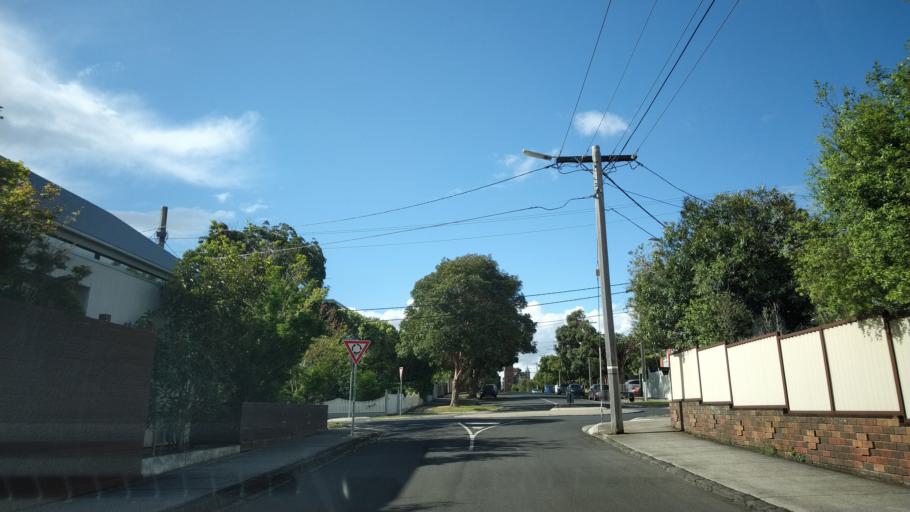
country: AU
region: Victoria
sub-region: Glen Eira
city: Caulfield
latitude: -37.8898
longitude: 145.0183
